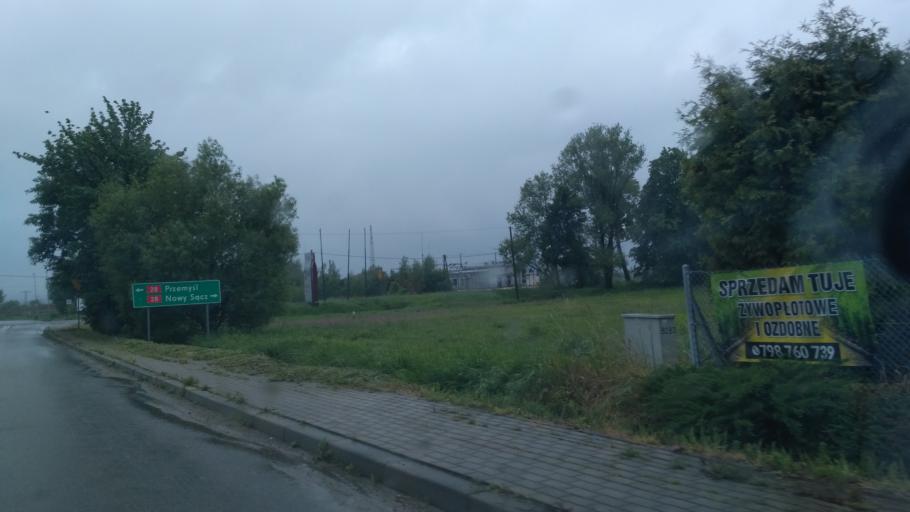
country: PL
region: Subcarpathian Voivodeship
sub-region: Powiat jasielski
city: Tarnowiec
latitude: 49.7612
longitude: 21.5399
